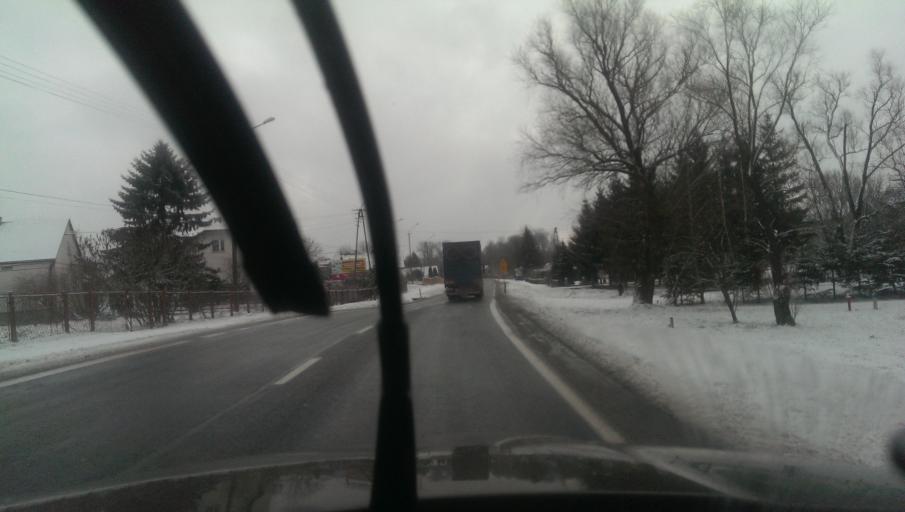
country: PL
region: Subcarpathian Voivodeship
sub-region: Powiat sanocki
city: Nowosielce-Gniewosz
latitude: 49.5600
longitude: 22.0923
